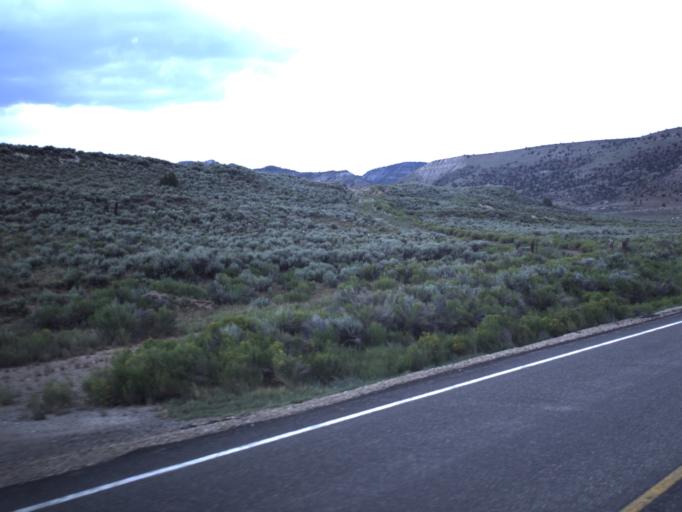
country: US
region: Utah
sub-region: Carbon County
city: Helper
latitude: 39.8042
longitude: -110.7811
